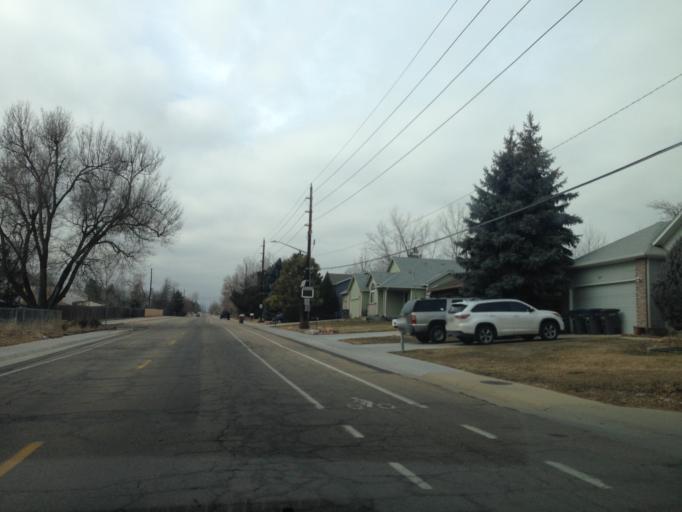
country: US
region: Colorado
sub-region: Boulder County
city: Lafayette
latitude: 39.9944
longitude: -105.0974
